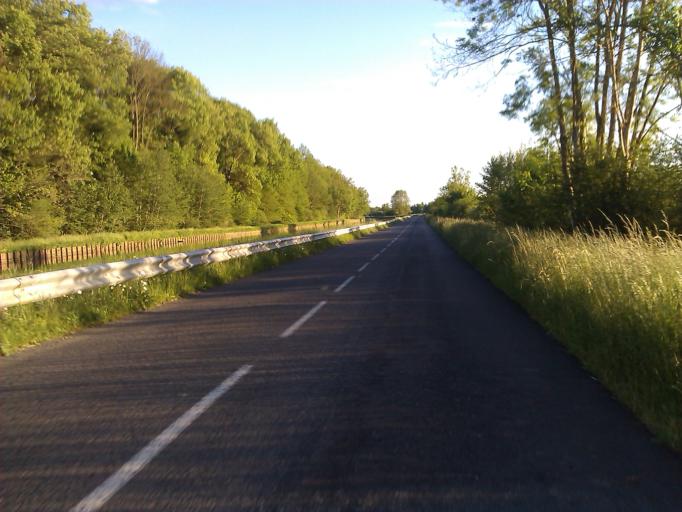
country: FR
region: Bourgogne
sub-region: Departement de Saone-et-Loire
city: Palinges
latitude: 46.5405
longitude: 4.2079
